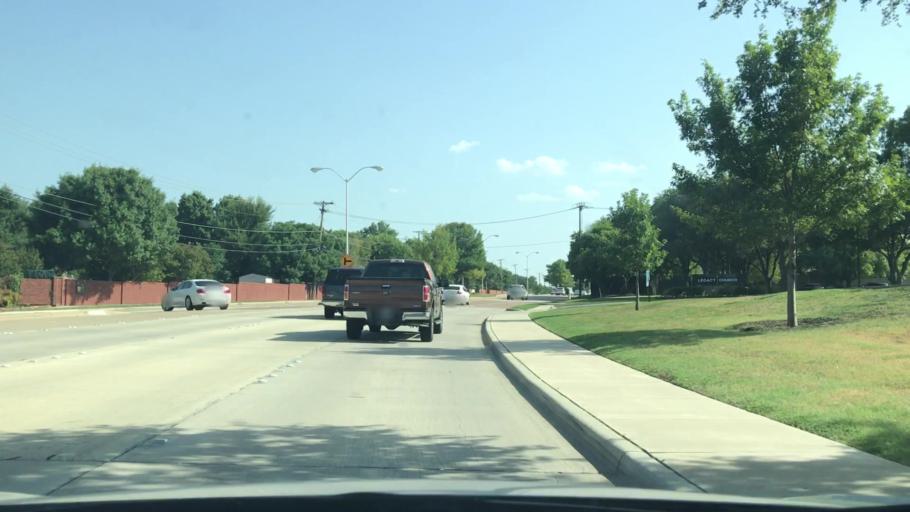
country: US
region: Texas
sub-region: Collin County
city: Plano
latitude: 33.0537
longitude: -96.7507
